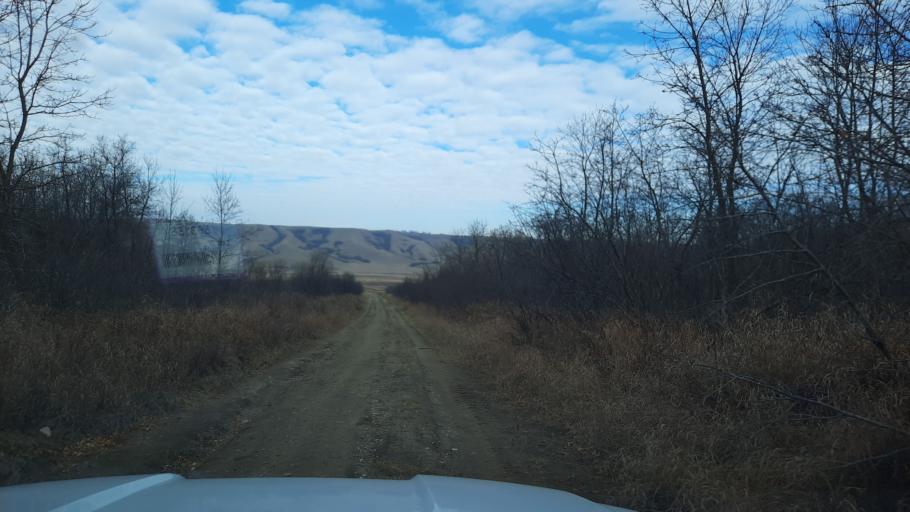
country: CA
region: Saskatchewan
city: Pilot Butte
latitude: 50.7812
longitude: -104.2084
